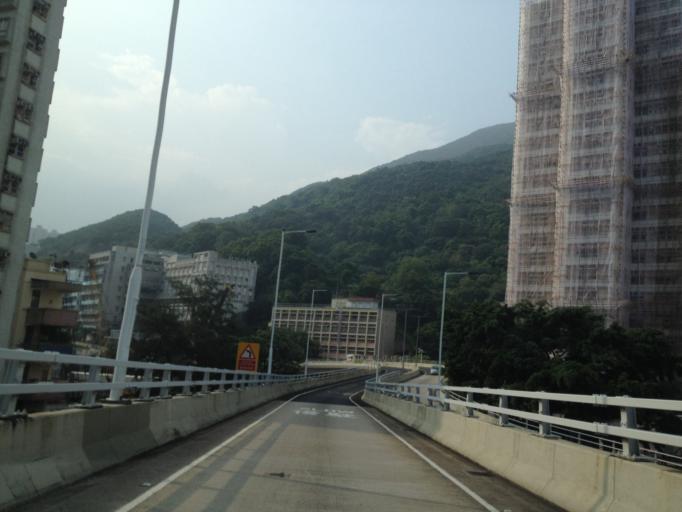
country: HK
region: Wanchai
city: Wan Chai
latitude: 22.2784
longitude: 114.2281
